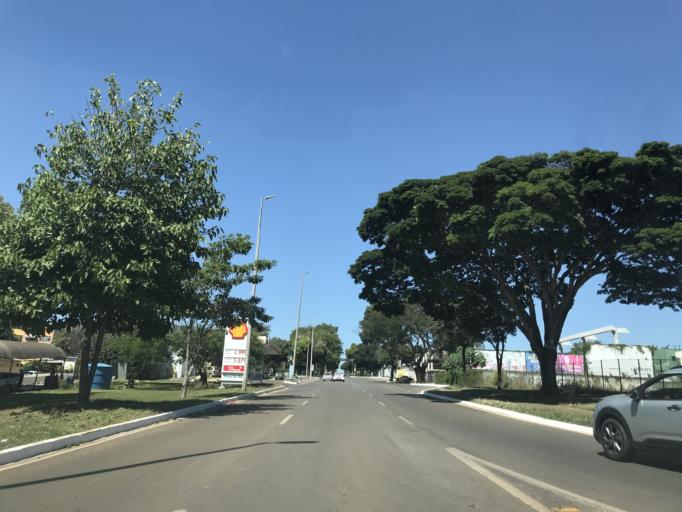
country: BR
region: Federal District
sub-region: Brasilia
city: Brasilia
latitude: -15.6460
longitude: -47.7871
